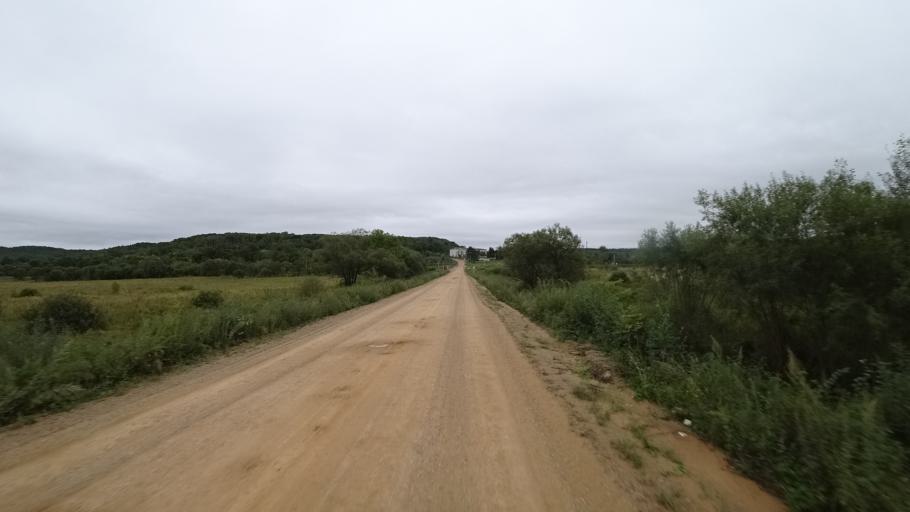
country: RU
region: Primorskiy
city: Rettikhovka
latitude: 44.1760
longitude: 132.8770
